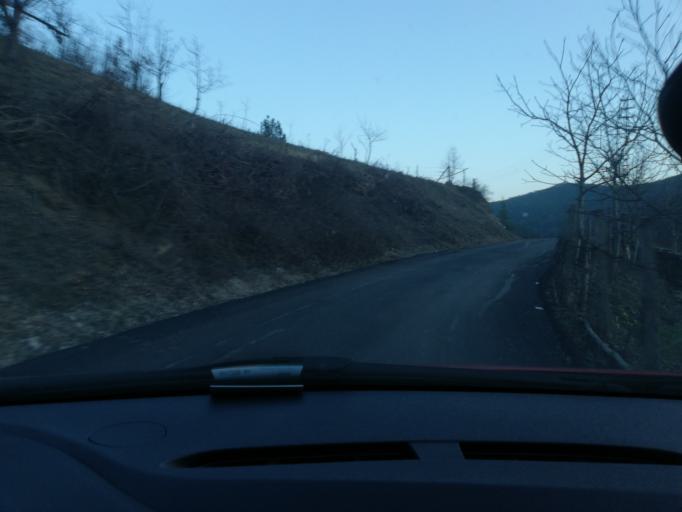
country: TR
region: Karabuk
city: Safranbolu
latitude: 41.2720
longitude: 32.6321
